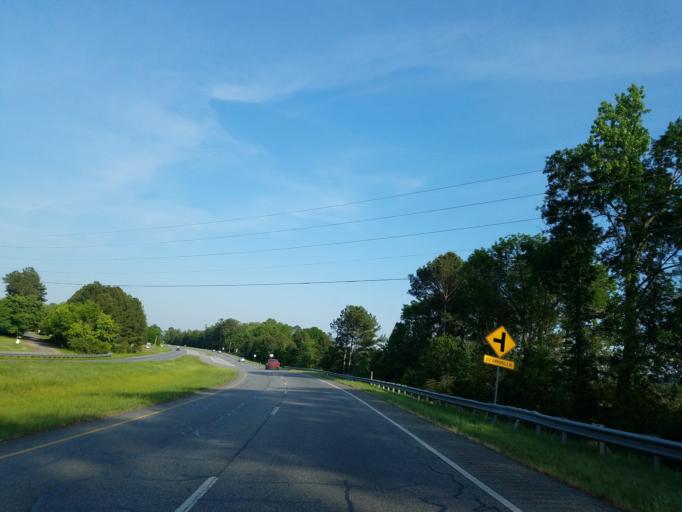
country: US
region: Georgia
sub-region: Floyd County
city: Rome
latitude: 34.4017
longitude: -85.2146
